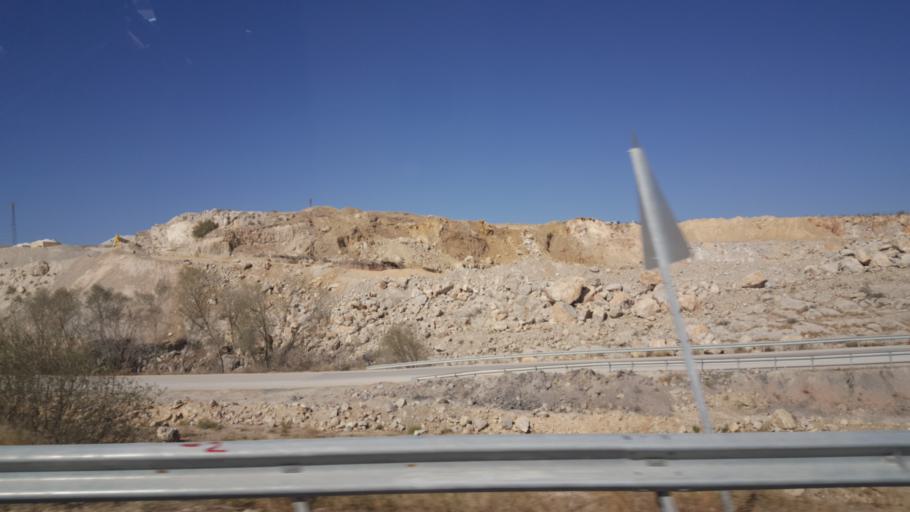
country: TR
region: Ankara
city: Ikizce
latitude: 39.6276
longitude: 32.7015
